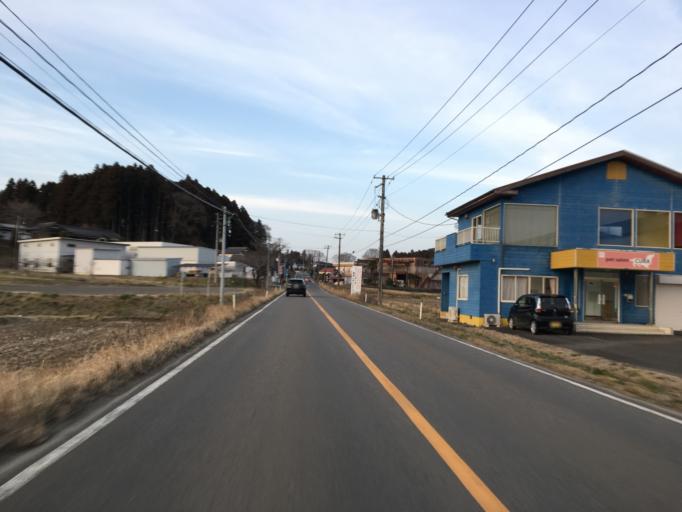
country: JP
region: Ibaraki
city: Daigo
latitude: 36.9465
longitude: 140.4075
